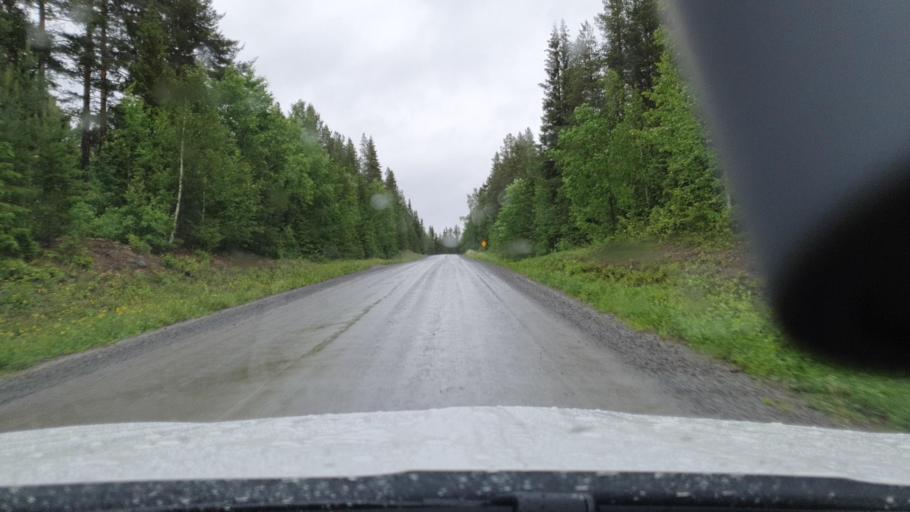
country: SE
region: Vaesterbotten
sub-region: Skelleftea Kommun
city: Burtraesk
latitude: 64.3683
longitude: 20.3943
